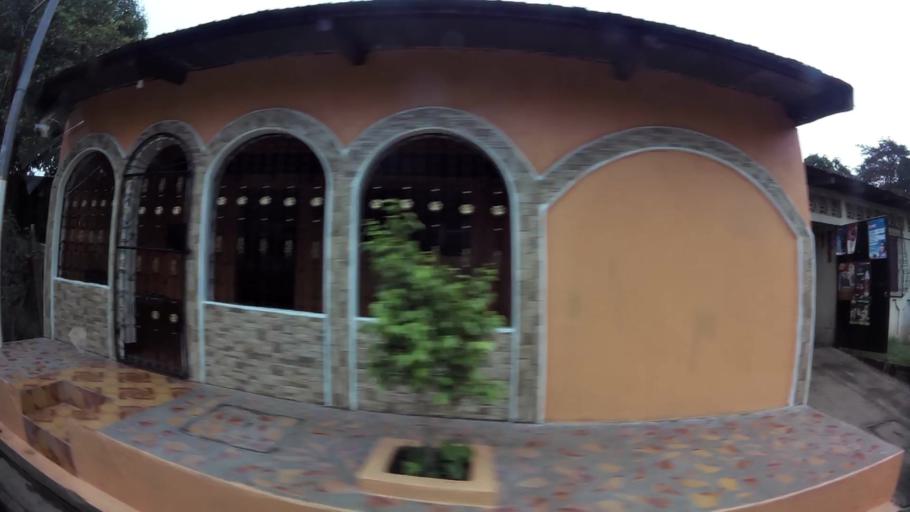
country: NI
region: Leon
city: Leon
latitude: 12.4504
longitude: -86.8662
